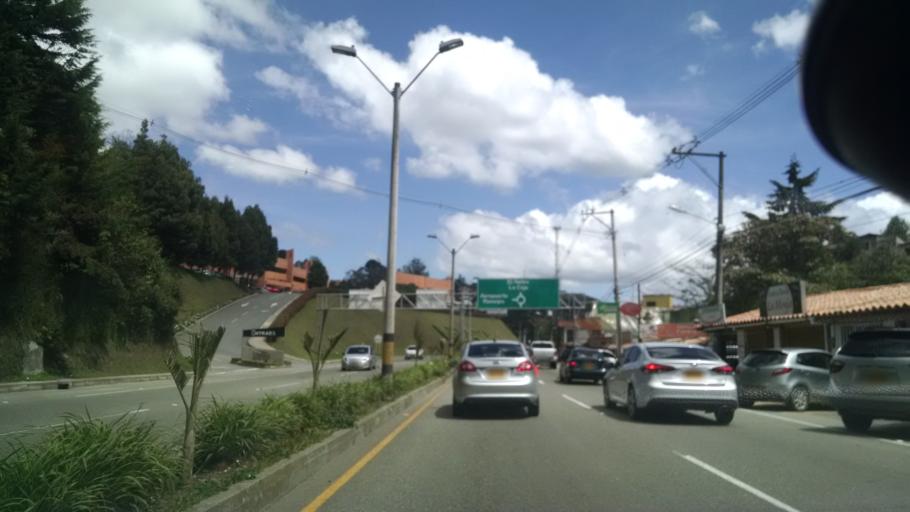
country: CO
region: Antioquia
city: Envigado
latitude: 6.1542
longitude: -75.5351
